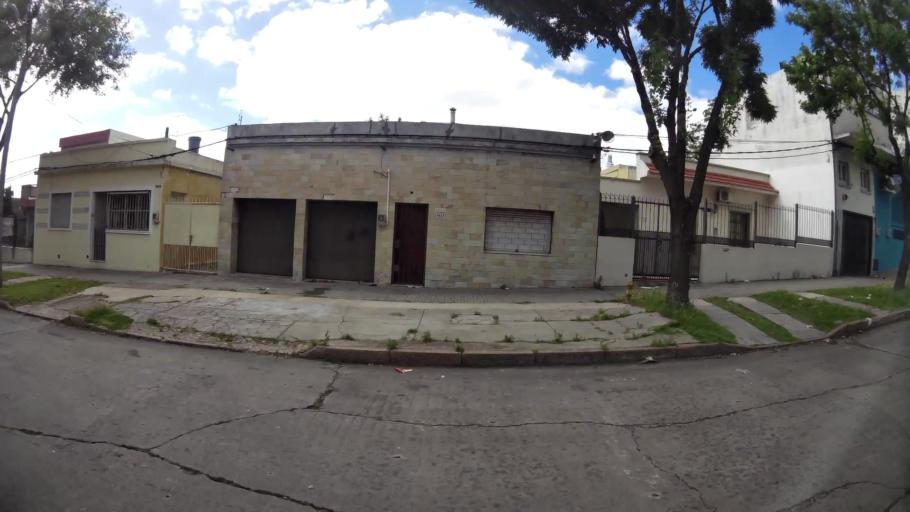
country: UY
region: Montevideo
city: Montevideo
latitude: -34.8855
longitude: -56.1388
